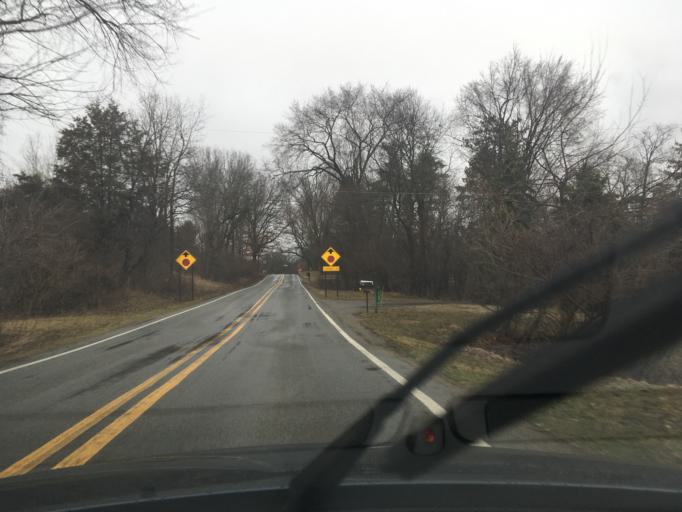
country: US
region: Michigan
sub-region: Washtenaw County
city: Chelsea
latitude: 42.3073
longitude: -84.0692
